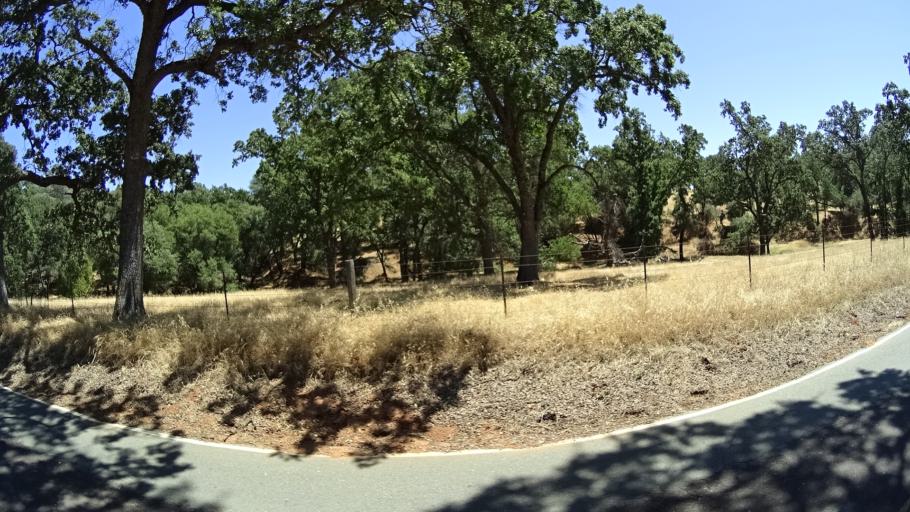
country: US
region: California
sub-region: Calaveras County
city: Murphys
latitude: 38.1235
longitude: -120.5059
